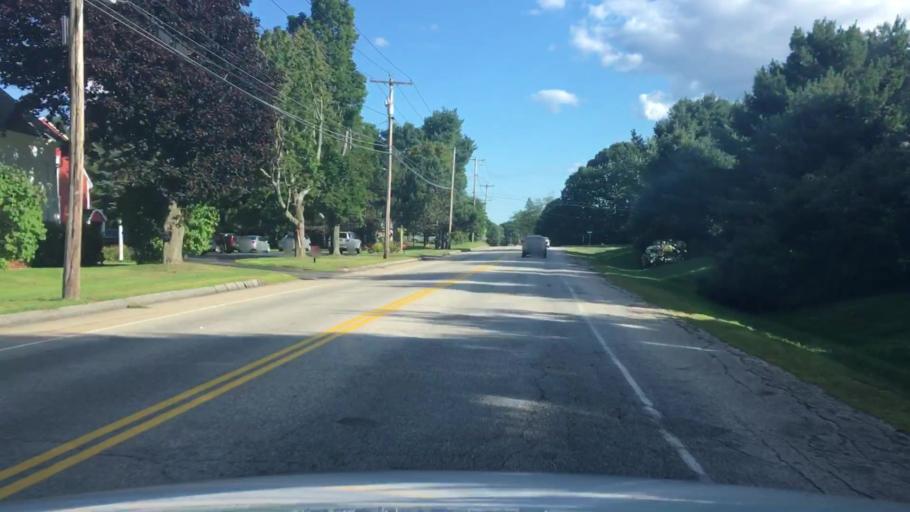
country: US
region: Maine
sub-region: Cumberland County
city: Scarborough
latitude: 43.5732
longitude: -70.3182
